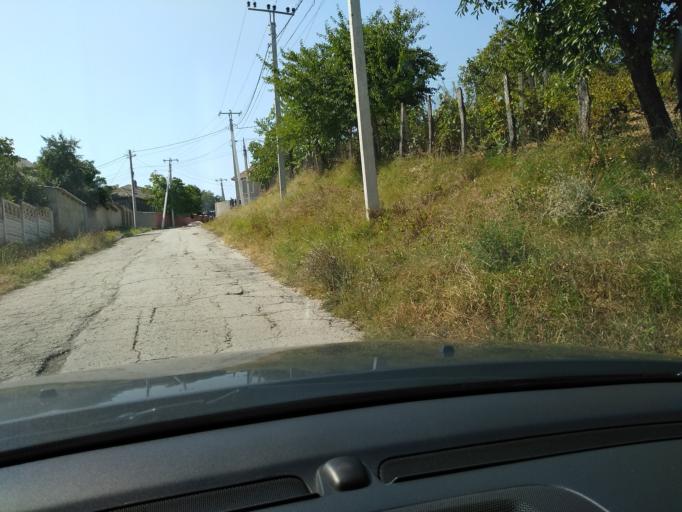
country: MD
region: Orhei
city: Orhei
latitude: 47.2601
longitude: 28.7679
